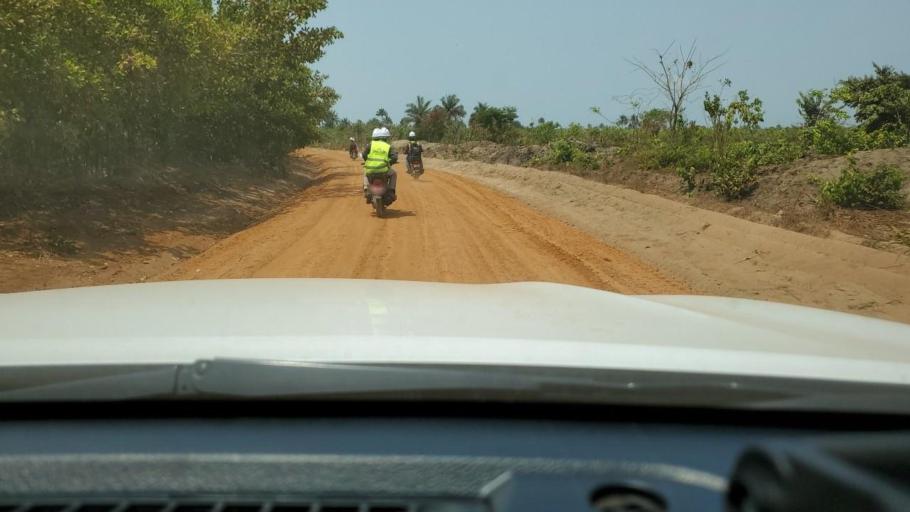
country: GN
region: Boke
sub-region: Boffa
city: Boffa
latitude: 10.0655
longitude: -13.8680
